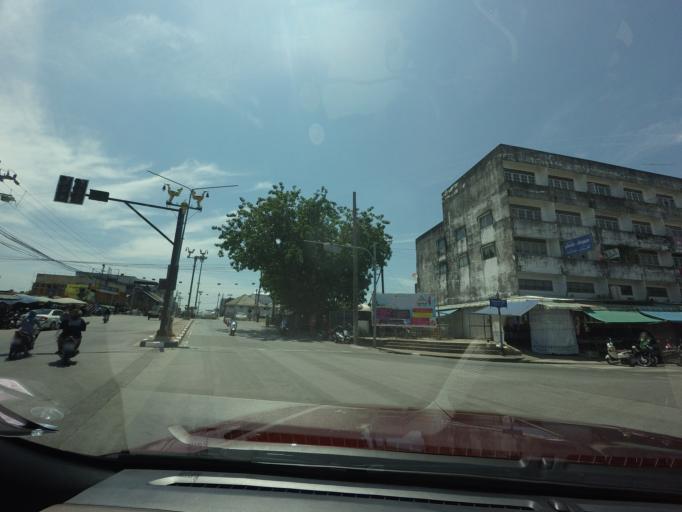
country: TH
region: Yala
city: Yala
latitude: 6.5619
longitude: 101.2916
